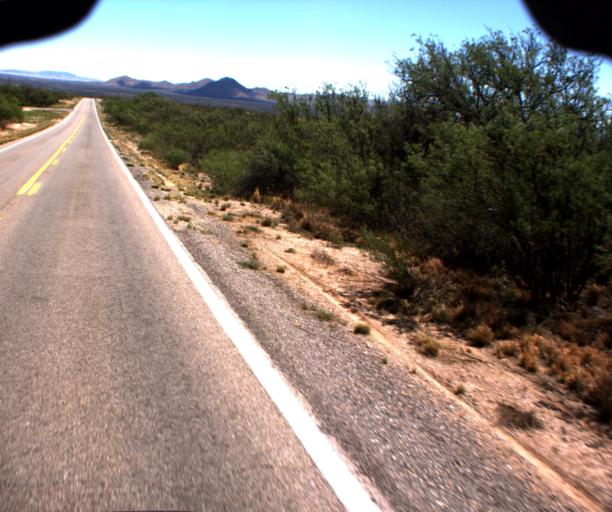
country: US
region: Arizona
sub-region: Cochise County
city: Huachuca City
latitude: 31.7204
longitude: -110.2267
